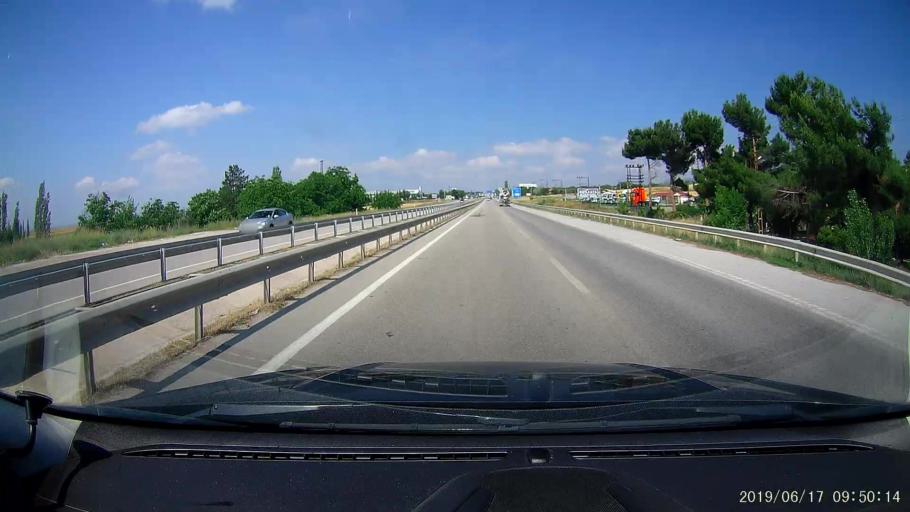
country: TR
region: Amasya
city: Merzifon
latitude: 40.8713
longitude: 35.5118
